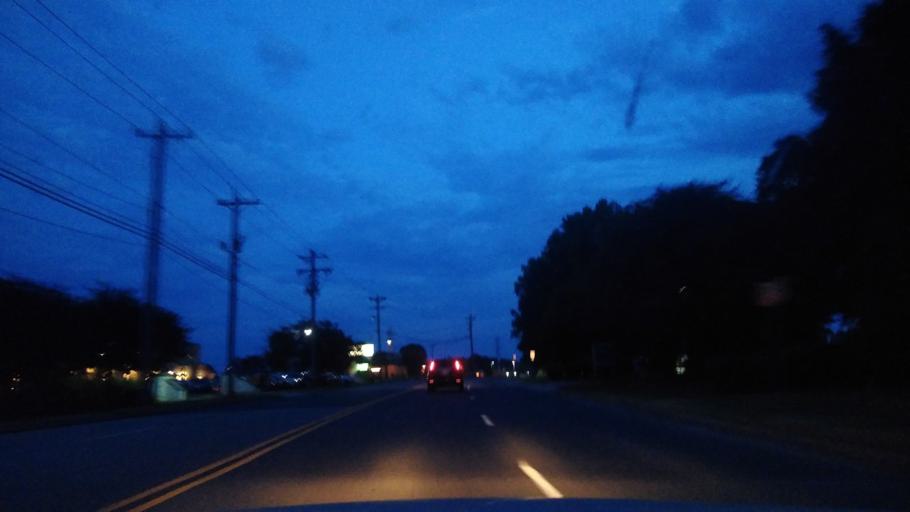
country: US
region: North Carolina
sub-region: Guilford County
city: Jamestown
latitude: 36.0652
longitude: -79.9097
